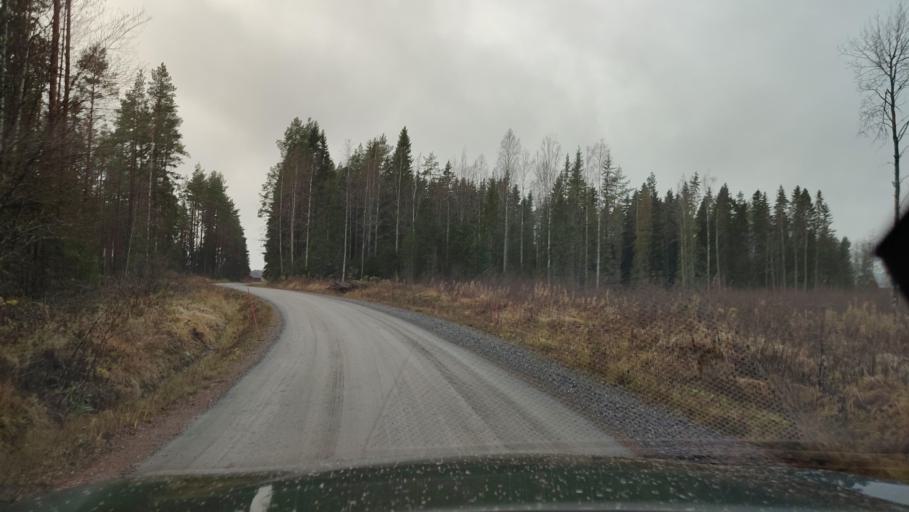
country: FI
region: Ostrobothnia
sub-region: Sydosterbotten
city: Naerpes
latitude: 62.4529
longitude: 21.4613
